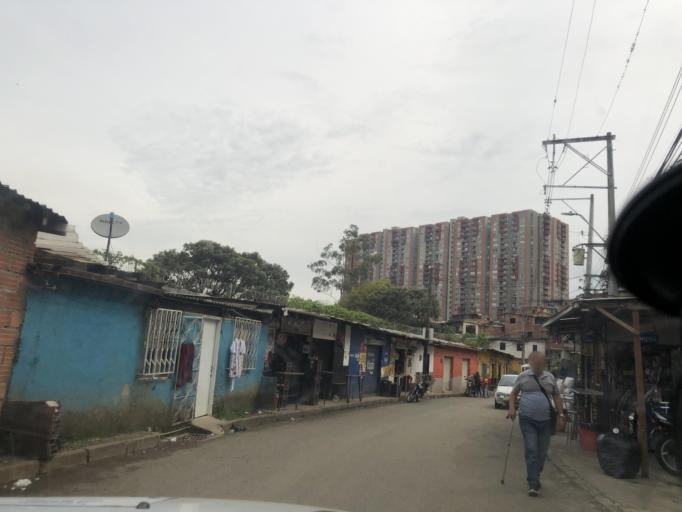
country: CO
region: Antioquia
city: Bello
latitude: 6.3292
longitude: -75.5426
